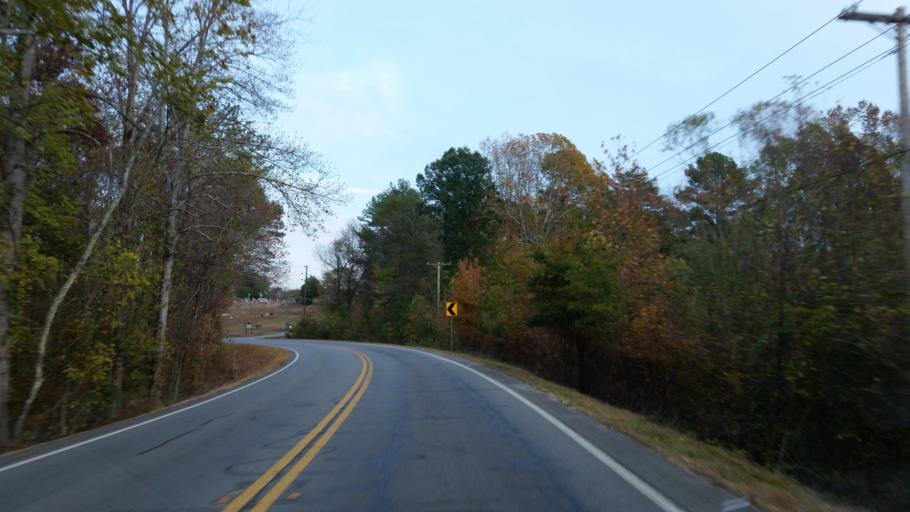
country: US
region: Georgia
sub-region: Gordon County
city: Calhoun
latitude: 34.5932
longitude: -84.8976
